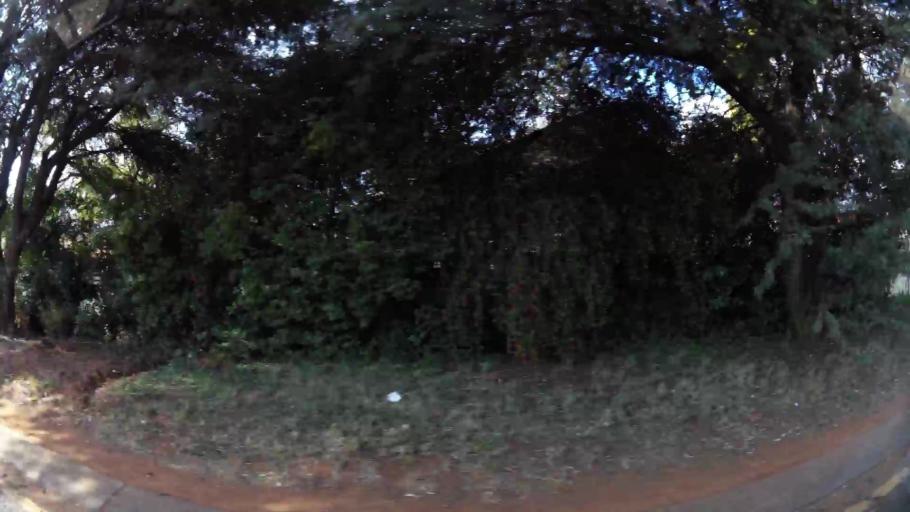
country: ZA
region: Gauteng
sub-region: City of Tshwane Metropolitan Municipality
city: Centurion
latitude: -25.8447
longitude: 28.2449
